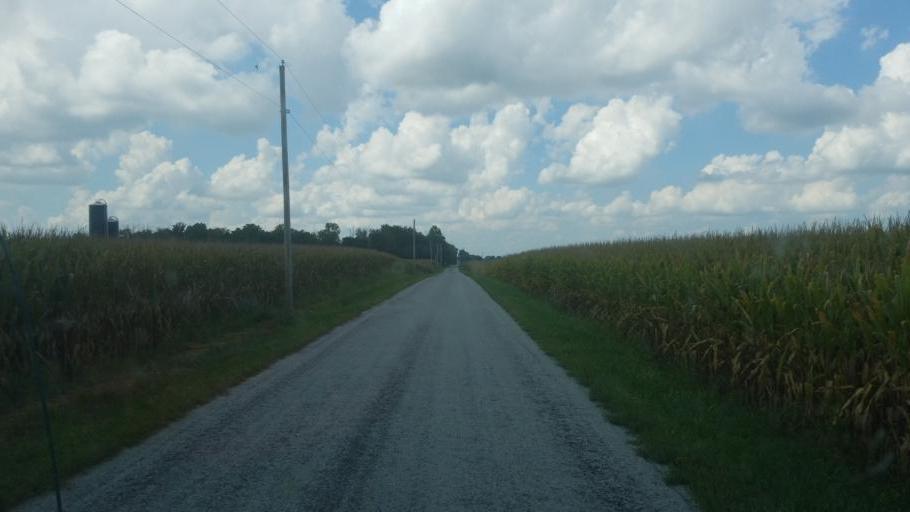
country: US
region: Ohio
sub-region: Hardin County
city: Kenton
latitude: 40.6881
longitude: -83.5692
